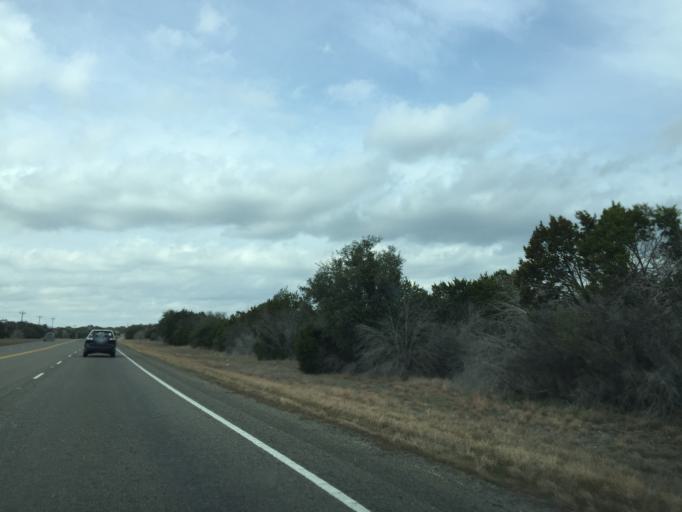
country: US
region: Texas
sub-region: Burnet County
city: Meadowlakes
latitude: 30.4965
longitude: -98.2580
